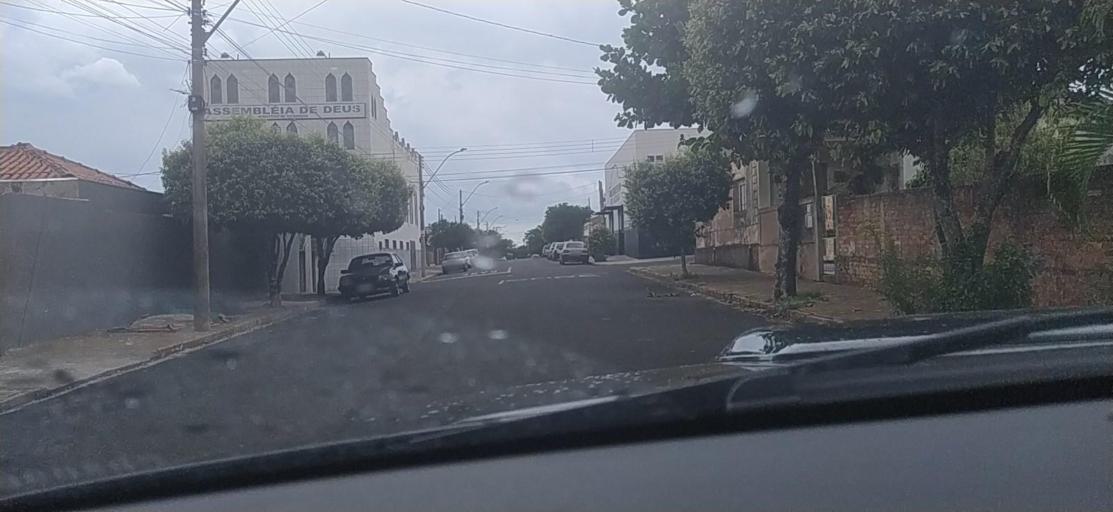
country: BR
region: Sao Paulo
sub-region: Pindorama
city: Pindorama
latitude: -21.1888
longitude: -48.9015
